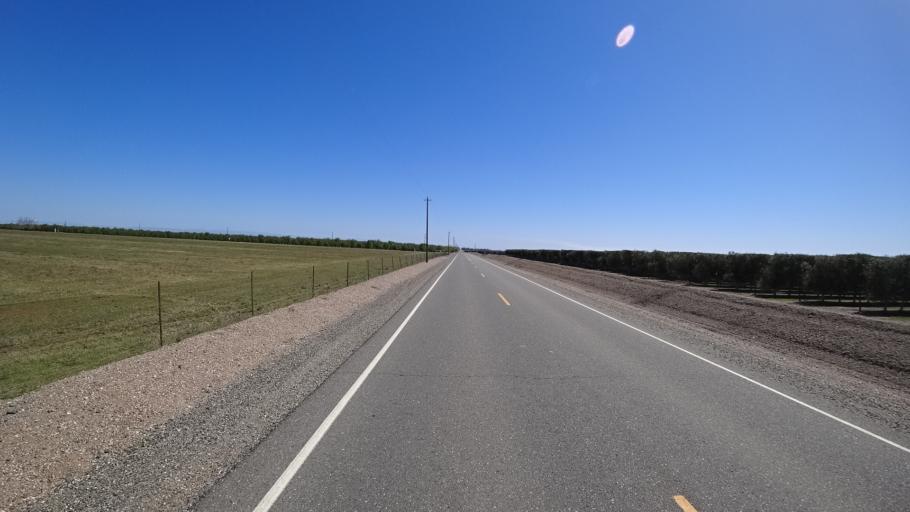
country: US
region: California
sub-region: Glenn County
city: Willows
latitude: 39.6246
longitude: -122.2374
